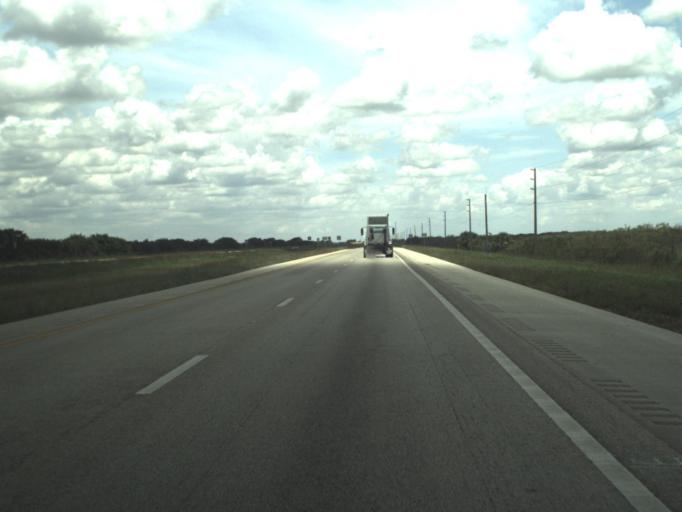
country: US
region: Florida
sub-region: Broward County
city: Weston
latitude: 26.1589
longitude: -80.7810
